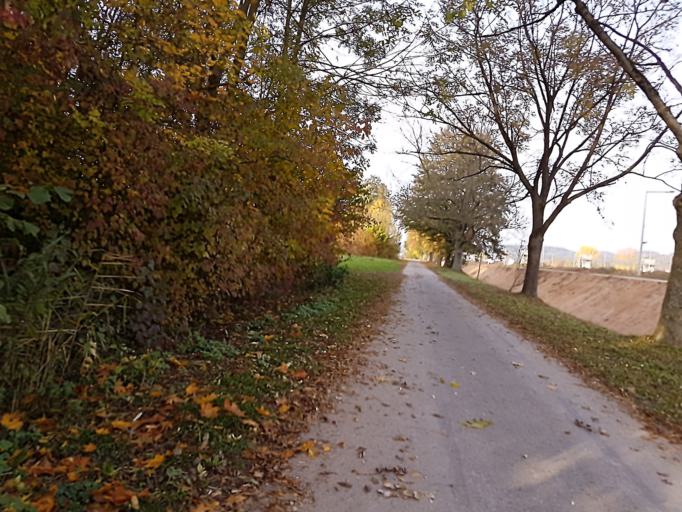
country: DE
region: Bavaria
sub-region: Regierungsbezirk Unterfranken
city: Kleinwallstadt
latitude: 49.8653
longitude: 9.1577
